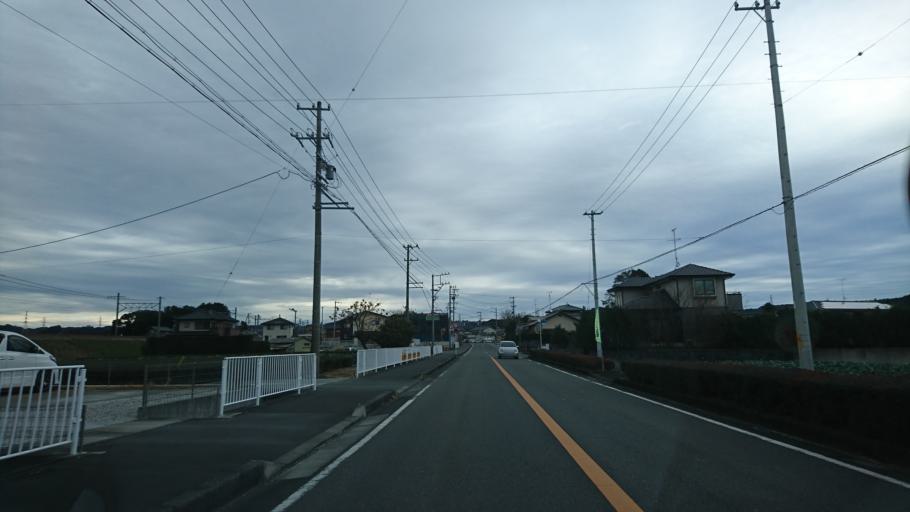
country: JP
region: Shizuoka
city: Kanaya
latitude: 34.7674
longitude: 138.1023
